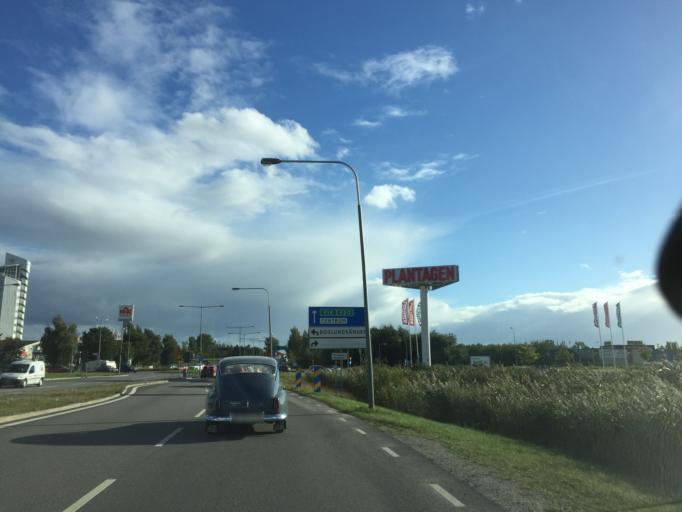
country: SE
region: OErebro
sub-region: Orebro Kommun
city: Orebro
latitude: 59.2985
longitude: 15.2011
